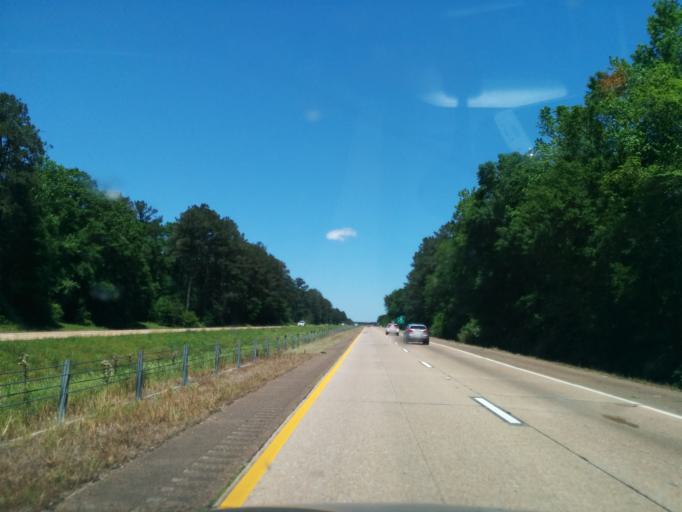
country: US
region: Mississippi
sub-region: Pike County
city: Magnolia
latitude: 31.1377
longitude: -90.4810
